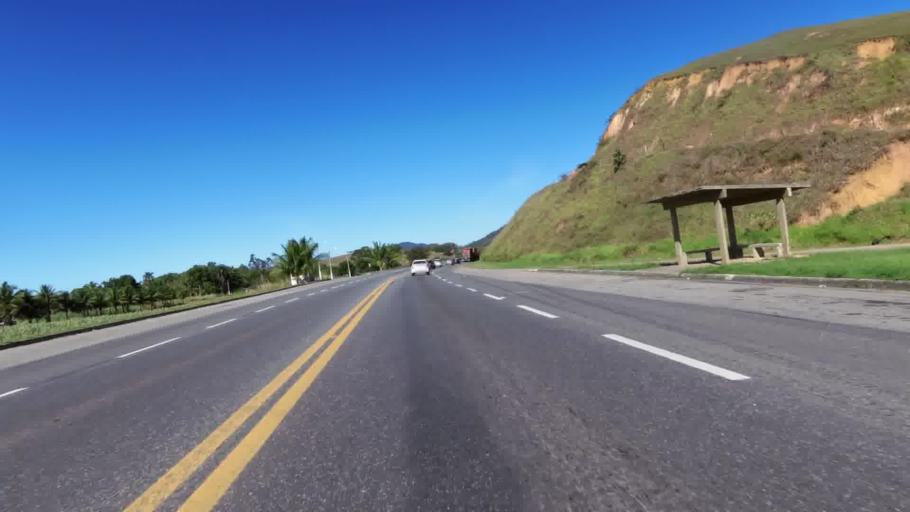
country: BR
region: Espirito Santo
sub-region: Alfredo Chaves
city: Alfredo Chaves
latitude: -20.6908
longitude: -40.6824
